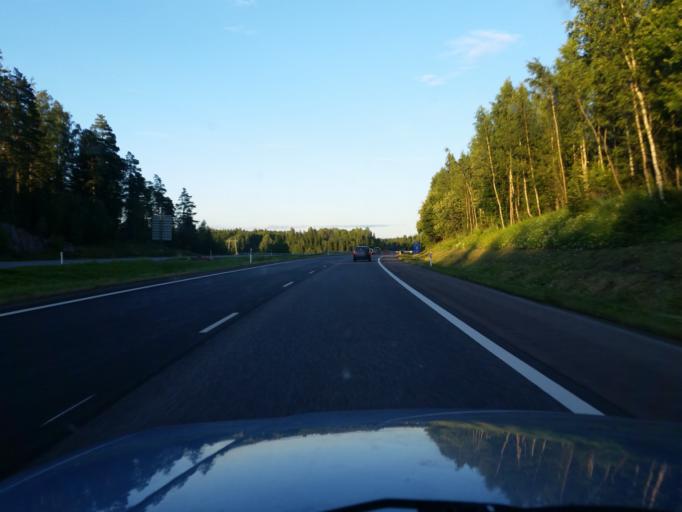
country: FI
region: Varsinais-Suomi
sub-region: Turku
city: Piikkioe
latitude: 60.4468
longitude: 22.5260
